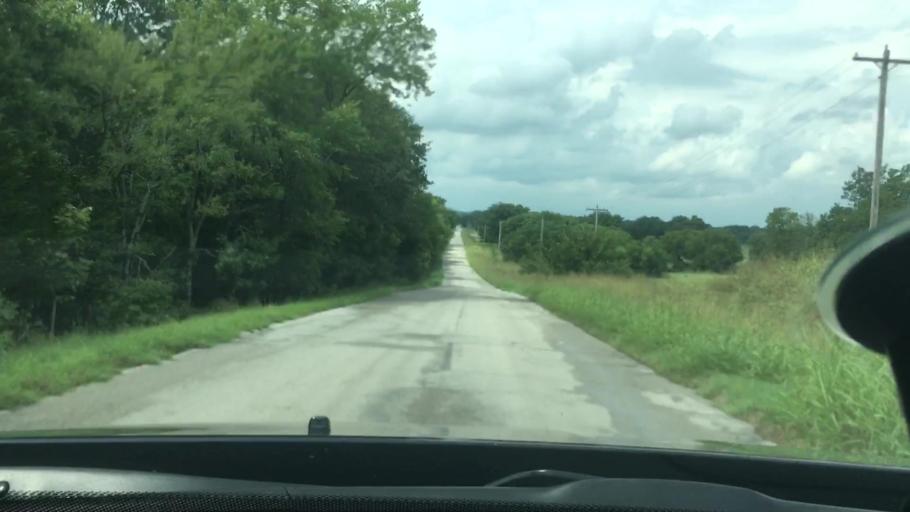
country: US
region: Oklahoma
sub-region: Carter County
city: Dickson
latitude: 34.2527
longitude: -96.9403
